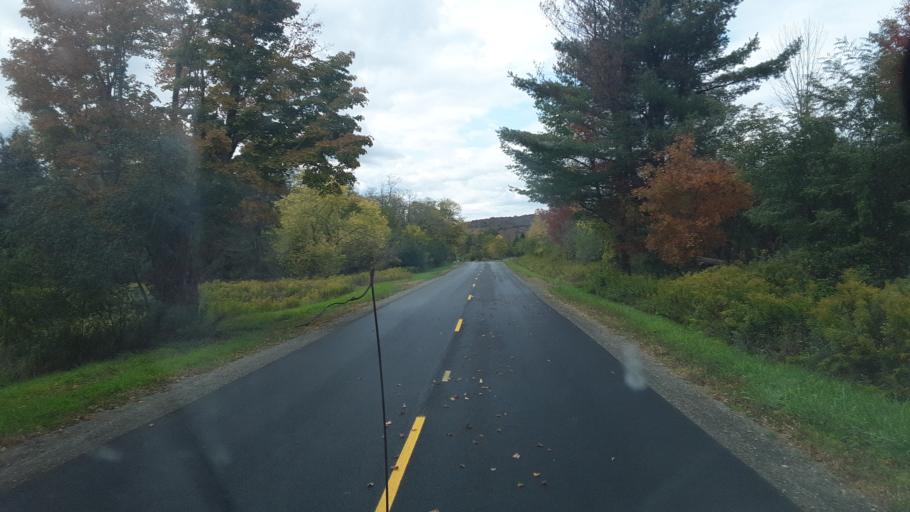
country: US
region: New York
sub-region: Allegany County
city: Alfred
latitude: 42.3696
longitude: -77.8014
